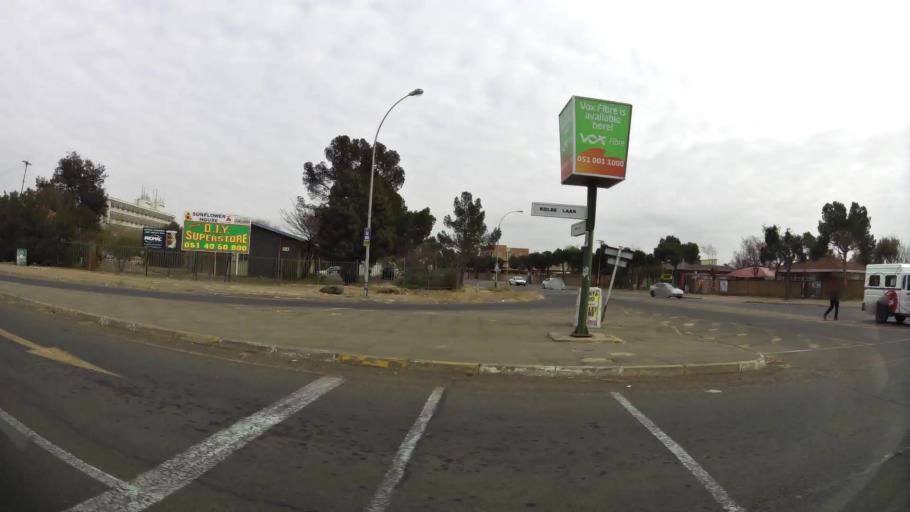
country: ZA
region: Orange Free State
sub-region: Mangaung Metropolitan Municipality
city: Bloemfontein
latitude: -29.1272
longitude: 26.2086
